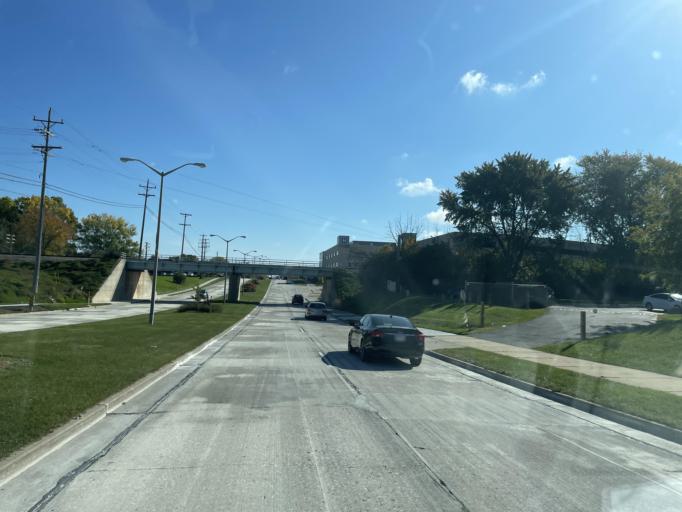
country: US
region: Wisconsin
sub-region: Milwaukee County
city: Oak Creek
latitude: 42.9014
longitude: -87.9233
